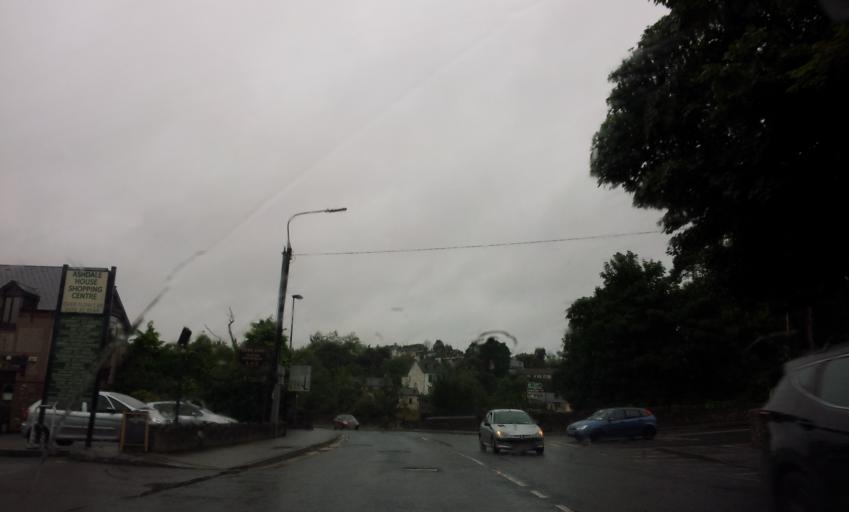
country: IE
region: Munster
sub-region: County Cork
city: Blarney
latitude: 51.9334
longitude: -8.5607
